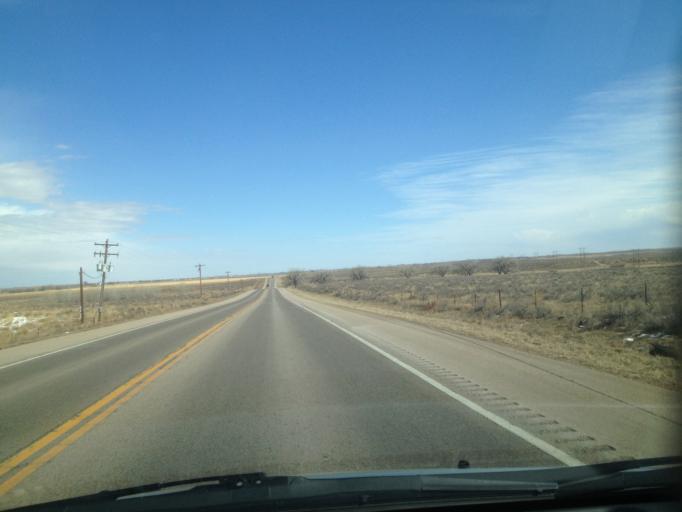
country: US
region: Colorado
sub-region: Weld County
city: Kersey
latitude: 40.2938
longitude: -104.3023
